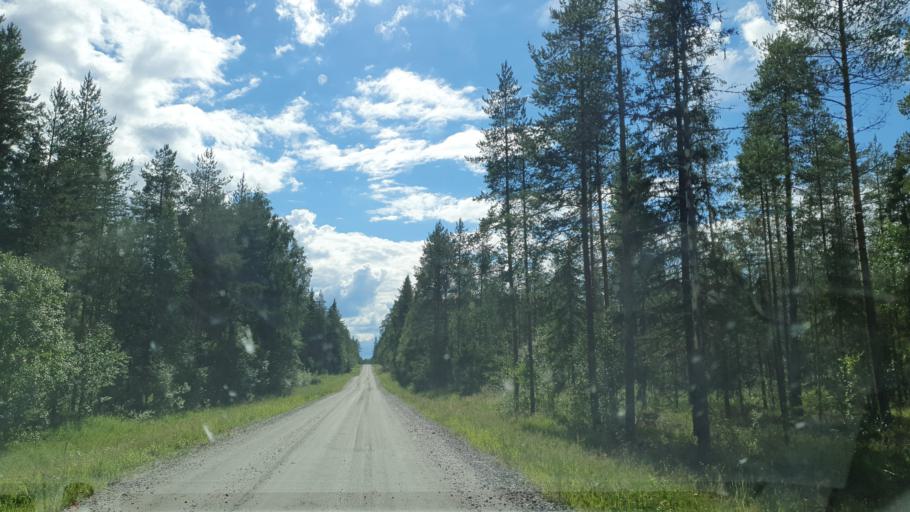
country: FI
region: Kainuu
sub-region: Kehys-Kainuu
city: Kuhmo
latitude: 64.1506
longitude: 29.7287
